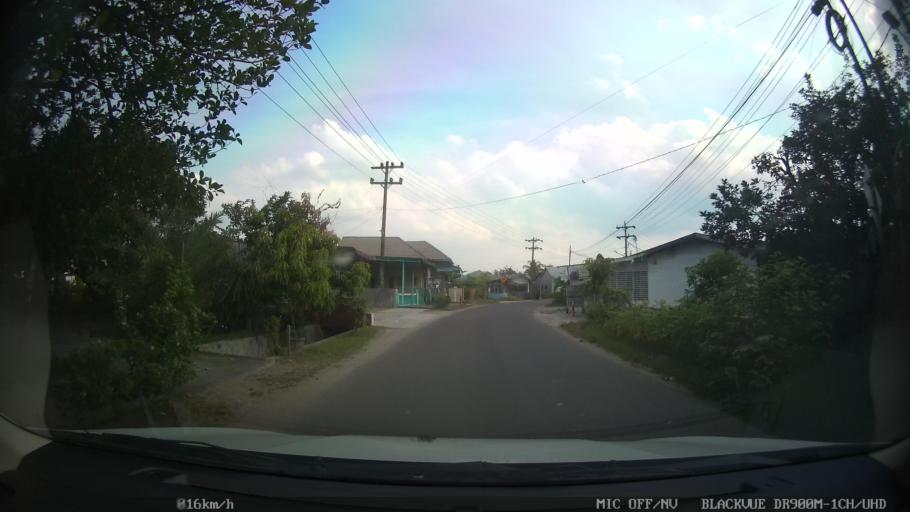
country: ID
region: North Sumatra
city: Binjai
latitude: 3.6442
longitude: 98.4977
